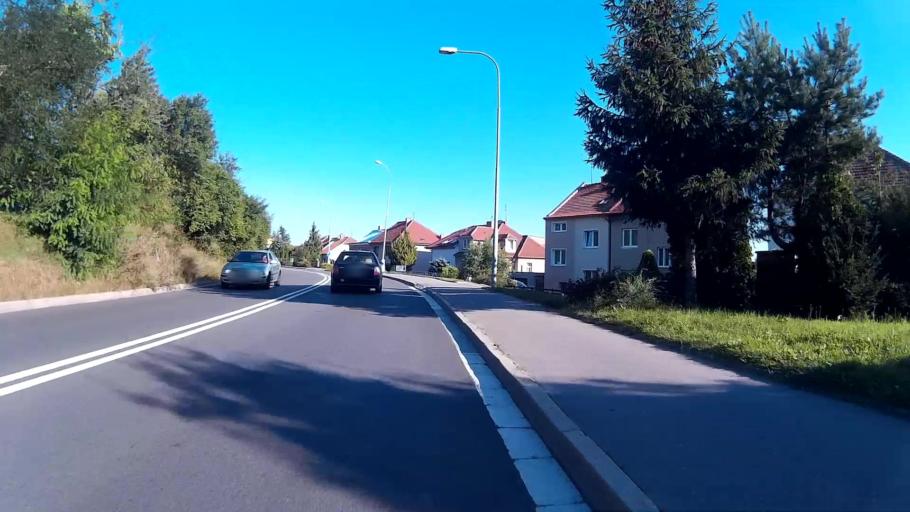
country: CZ
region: South Moravian
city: Moravany
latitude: 49.1650
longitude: 16.5877
